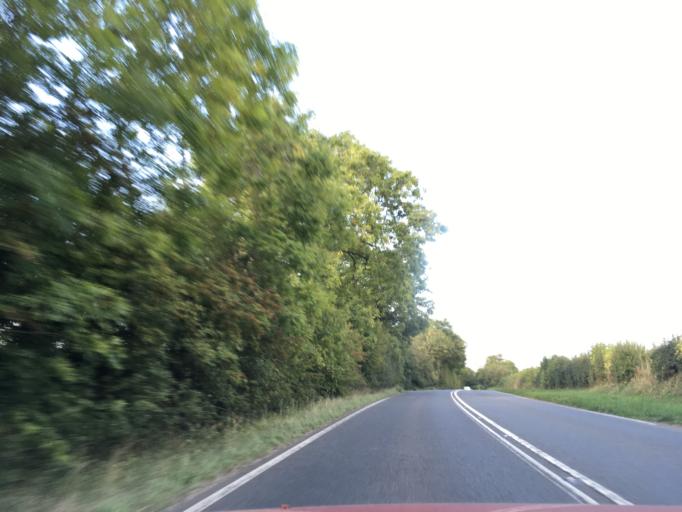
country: GB
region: England
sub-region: Gloucestershire
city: Bourton on the Water
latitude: 51.8696
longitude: -1.7916
